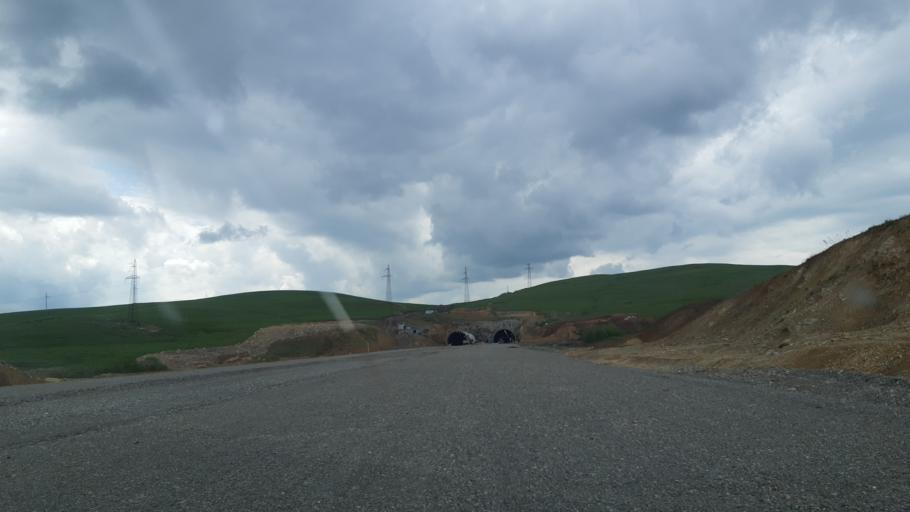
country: KZ
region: Ongtustik Qazaqstan
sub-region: Tulkibas Audany
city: Zhabagly
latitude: 42.5219
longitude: 70.5808
